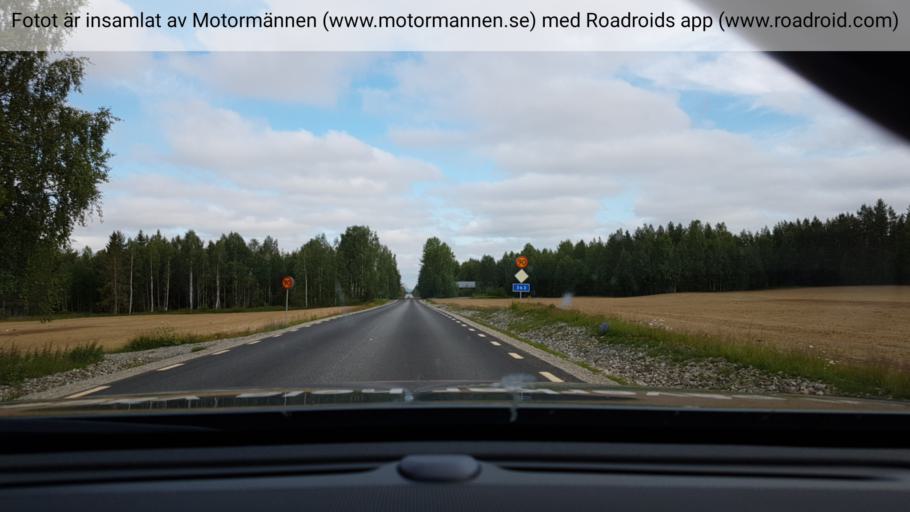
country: SE
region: Vaesterbotten
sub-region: Norsjo Kommun
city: Norsjoe
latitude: 64.5420
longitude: 19.3353
